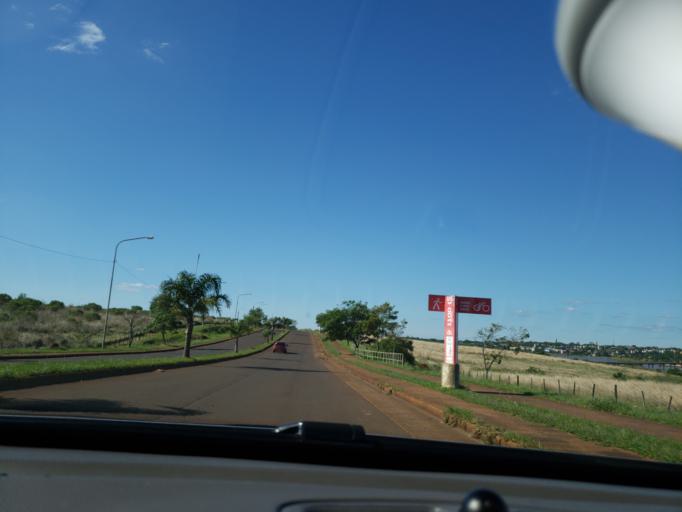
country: AR
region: Misiones
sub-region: Departamento de Capital
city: Posadas
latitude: -27.3888
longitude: -55.9618
